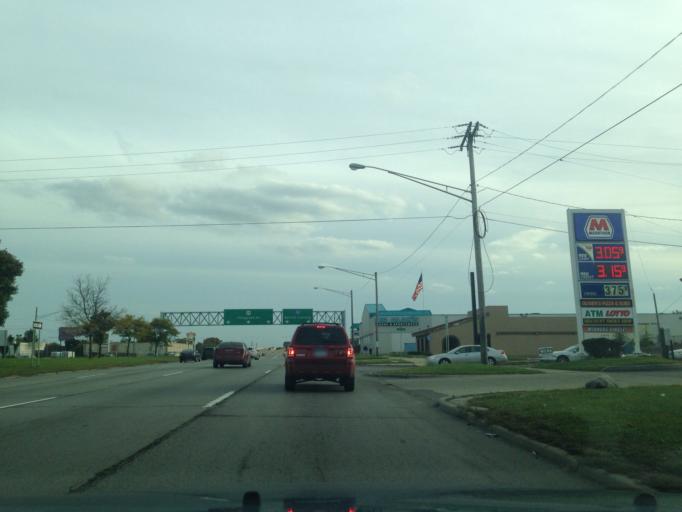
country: US
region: Michigan
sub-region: Wayne County
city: Redford
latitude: 42.3909
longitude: -83.2767
